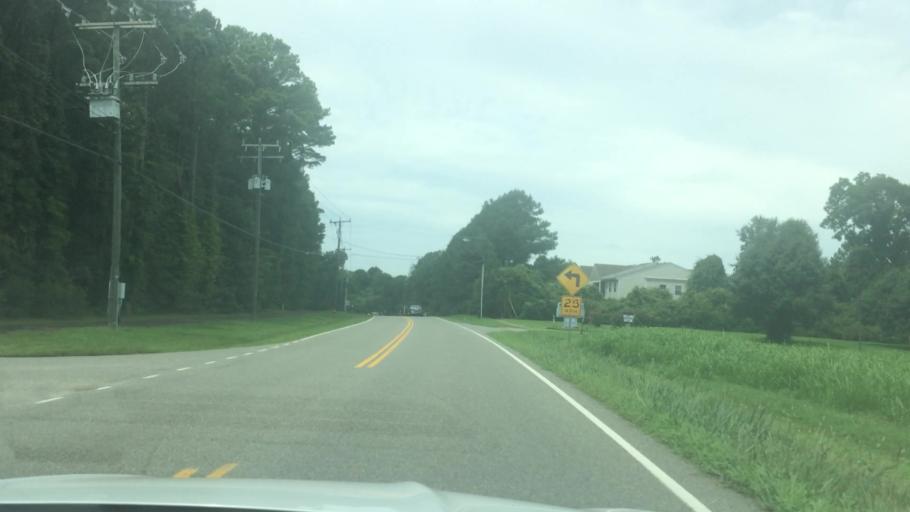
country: US
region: Virginia
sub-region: James City County
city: Williamsburg
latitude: 37.2983
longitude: -76.7373
